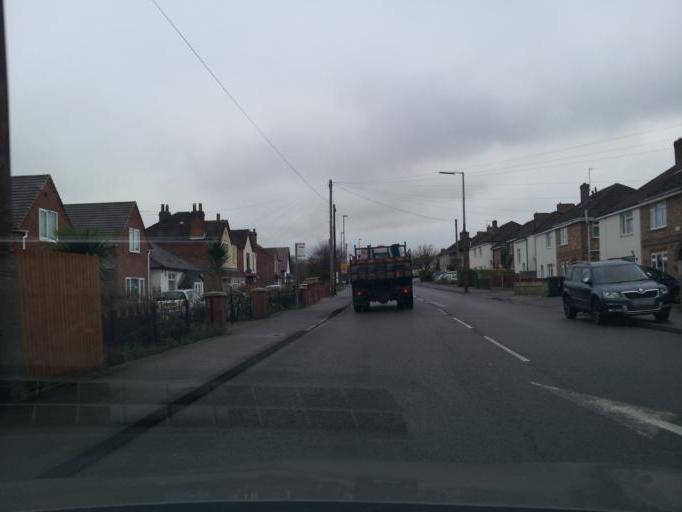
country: GB
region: England
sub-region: Derbyshire
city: Swadlincote
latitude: 52.7776
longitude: -1.5401
